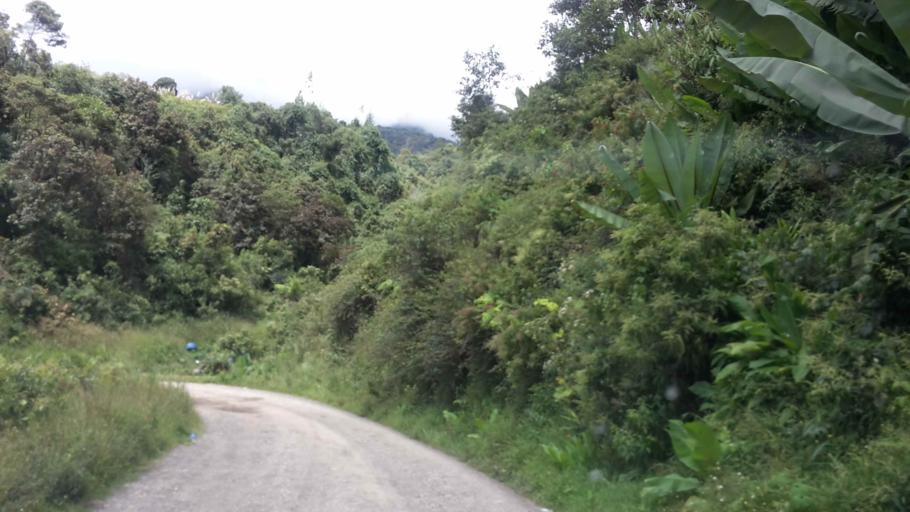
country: BO
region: Cochabamba
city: Colomi
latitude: -17.1300
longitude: -65.9357
